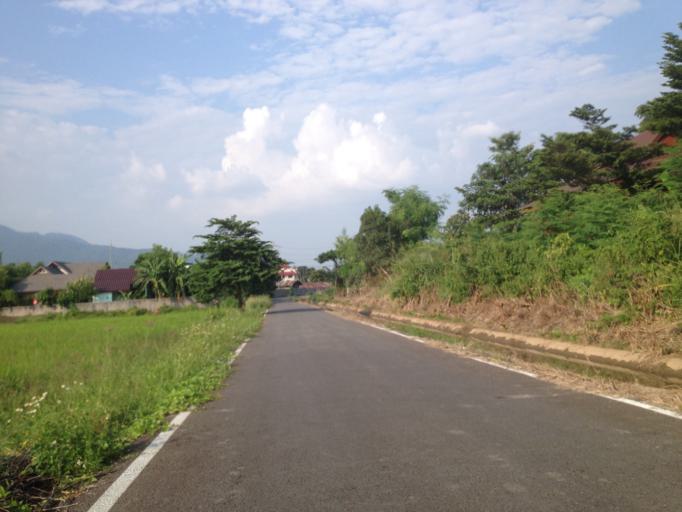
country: TH
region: Chiang Mai
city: Hang Dong
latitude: 18.7326
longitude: 98.9288
